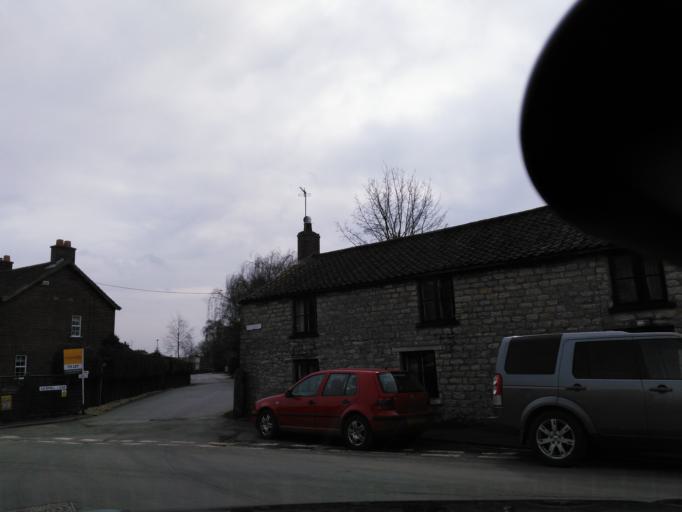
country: GB
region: England
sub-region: North Yorkshire
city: Helmsley
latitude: 54.2447
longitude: -1.0574
